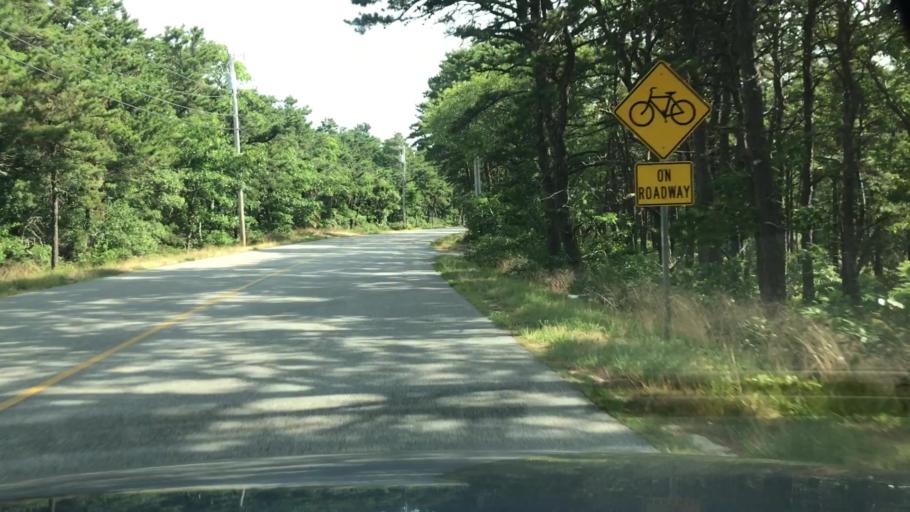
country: US
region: Massachusetts
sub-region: Barnstable County
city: Truro
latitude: 42.0287
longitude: -70.0685
